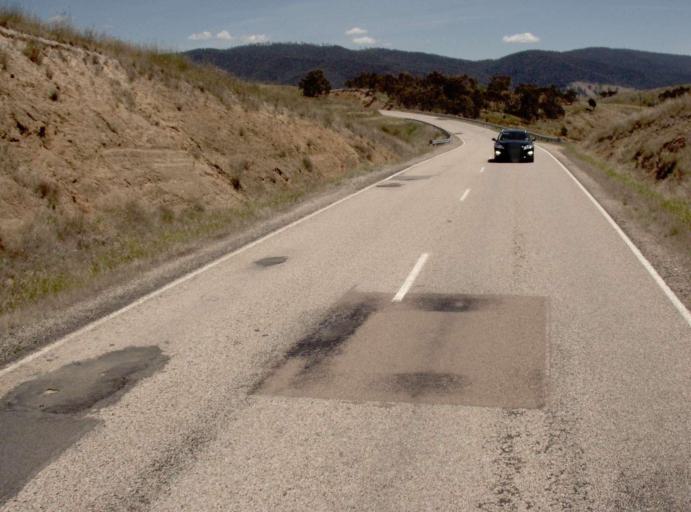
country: AU
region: Victoria
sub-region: Alpine
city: Mount Beauty
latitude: -37.1196
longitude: 147.6218
